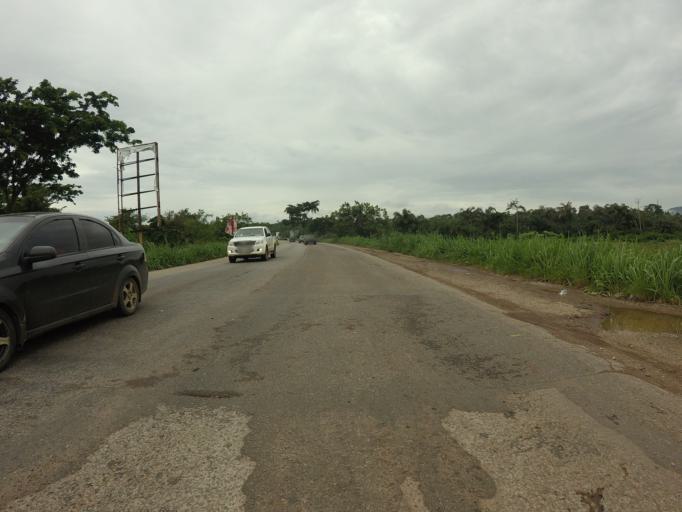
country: GH
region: Eastern
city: Begoro
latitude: 6.3875
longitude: -0.5536
